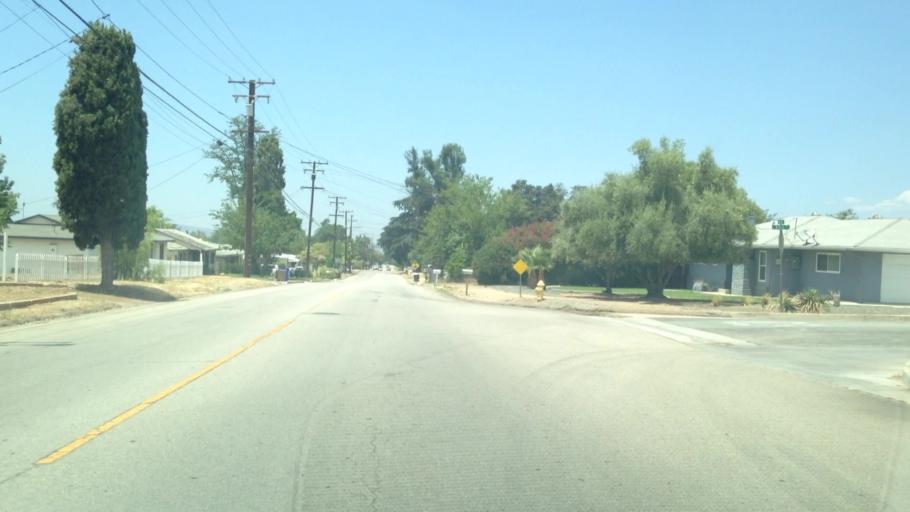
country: US
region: California
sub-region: San Bernardino County
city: Yucaipa
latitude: 34.0267
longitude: -117.0447
